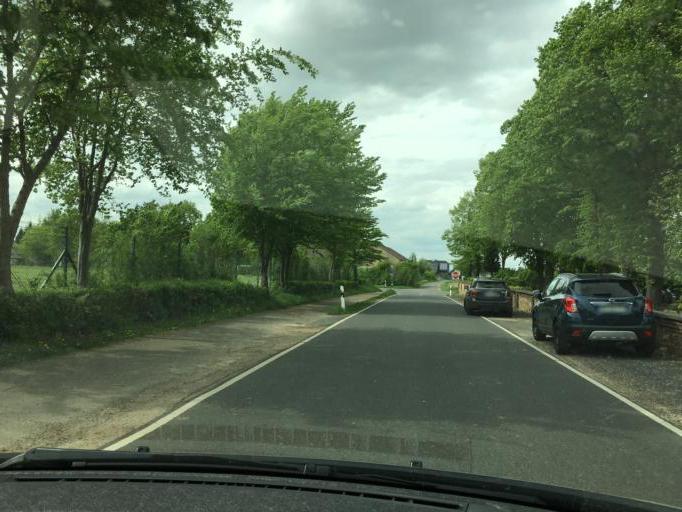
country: DE
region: North Rhine-Westphalia
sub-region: Regierungsbezirk Koln
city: Merzenich
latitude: 50.7934
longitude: 6.5449
